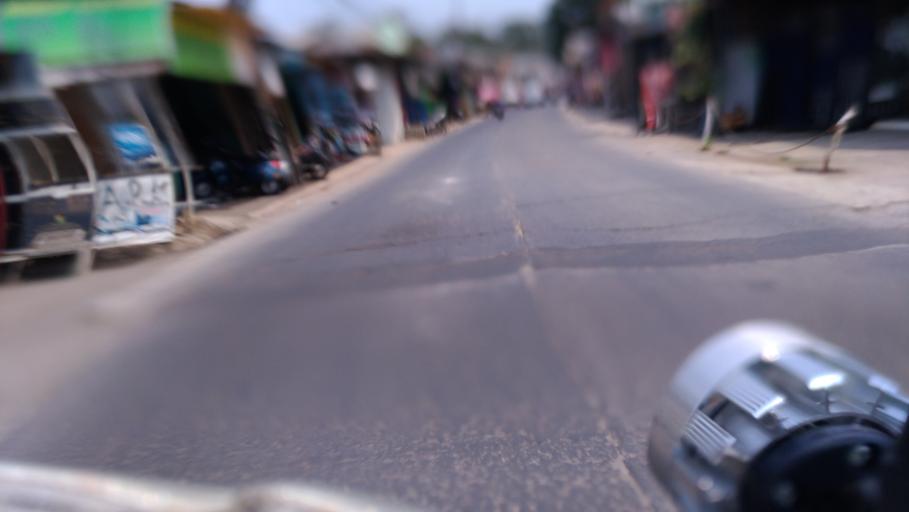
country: ID
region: West Java
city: Cileungsir
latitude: -6.3579
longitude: 106.9099
